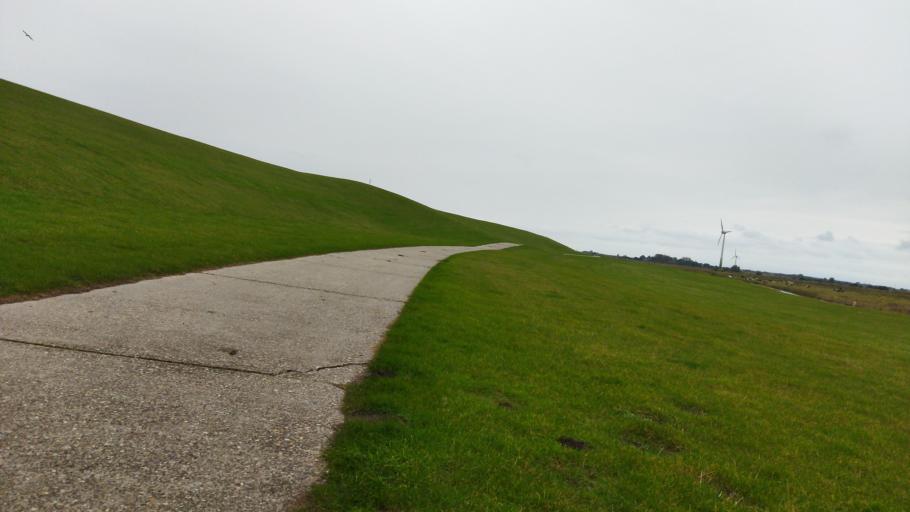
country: DE
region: Lower Saxony
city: Hinte
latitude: 53.4861
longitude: 7.0320
